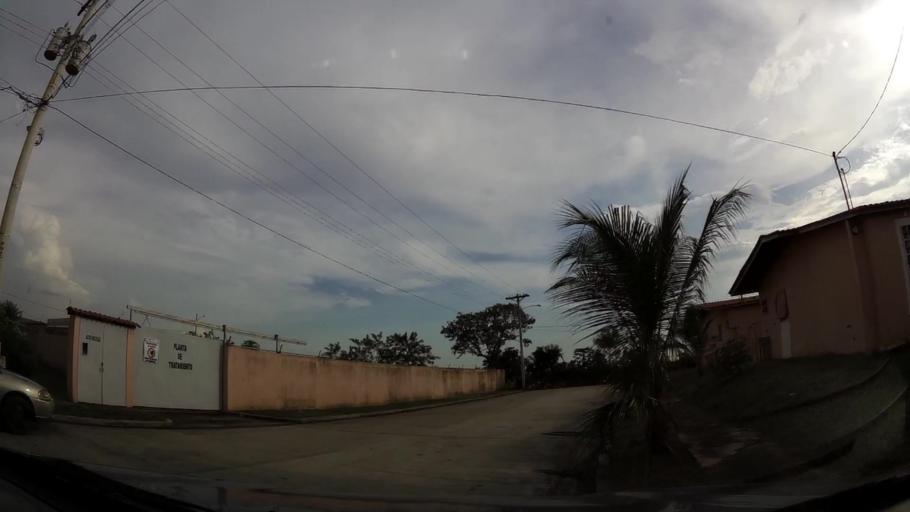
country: PA
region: Panama
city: Tocumen
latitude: 9.0686
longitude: -79.3619
